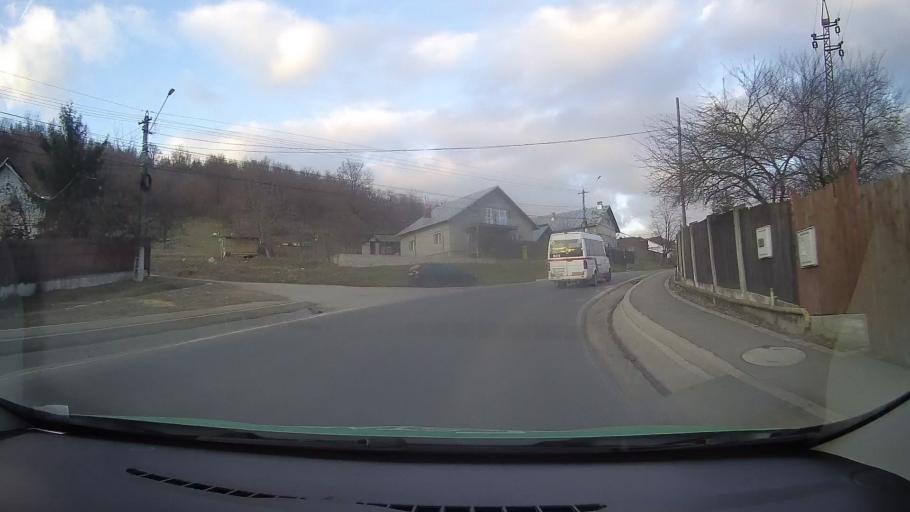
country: RO
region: Dambovita
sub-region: Municipiul Moreni
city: Moreni
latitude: 44.9781
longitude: 25.6204
